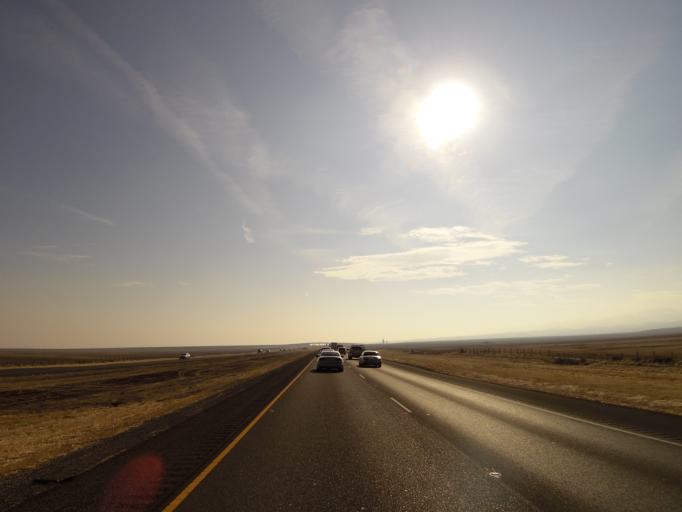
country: US
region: California
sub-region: Fresno County
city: Mendota
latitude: 36.5875
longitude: -120.5636
